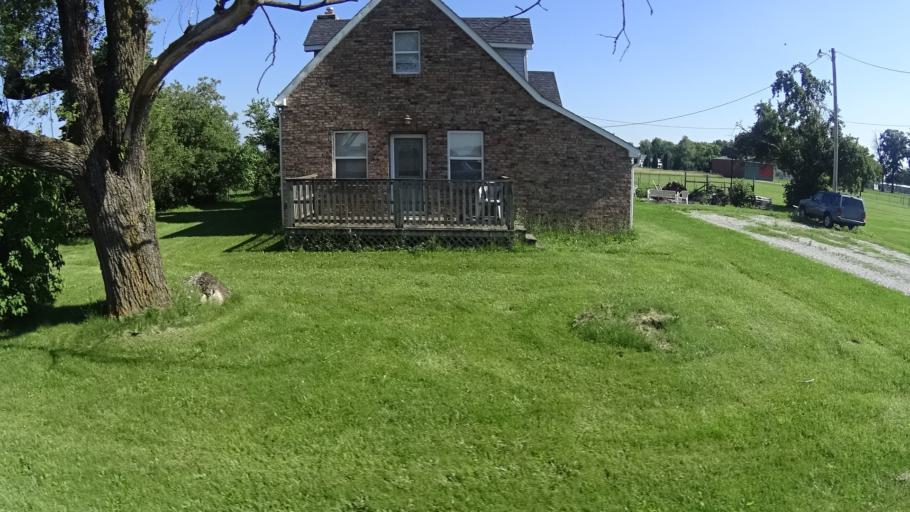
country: US
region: Indiana
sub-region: Madison County
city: Ingalls
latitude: 39.9878
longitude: -85.8401
